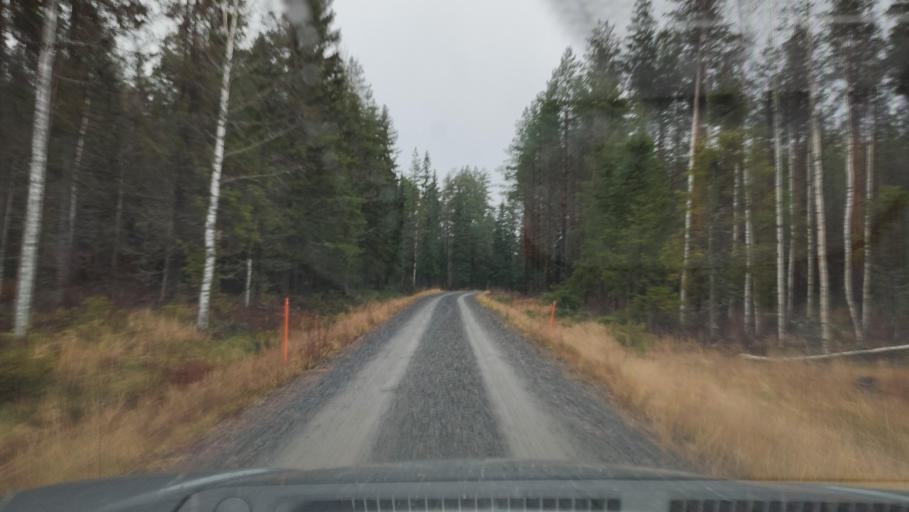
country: FI
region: Southern Ostrobothnia
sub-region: Suupohja
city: Karijoki
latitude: 62.1379
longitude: 21.6269
